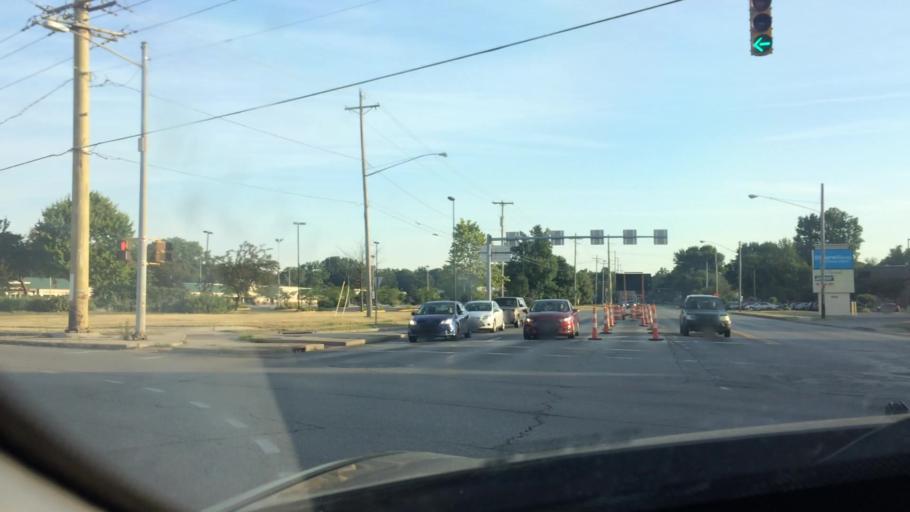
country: US
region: Ohio
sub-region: Lucas County
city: Ottawa Hills
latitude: 41.6991
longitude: -83.6449
